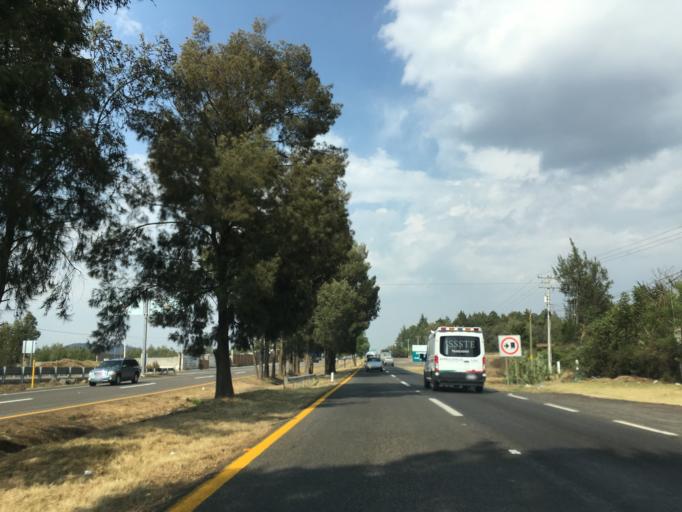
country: MX
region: Michoacan
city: Patzcuaro
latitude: 19.5326
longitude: -101.5535
